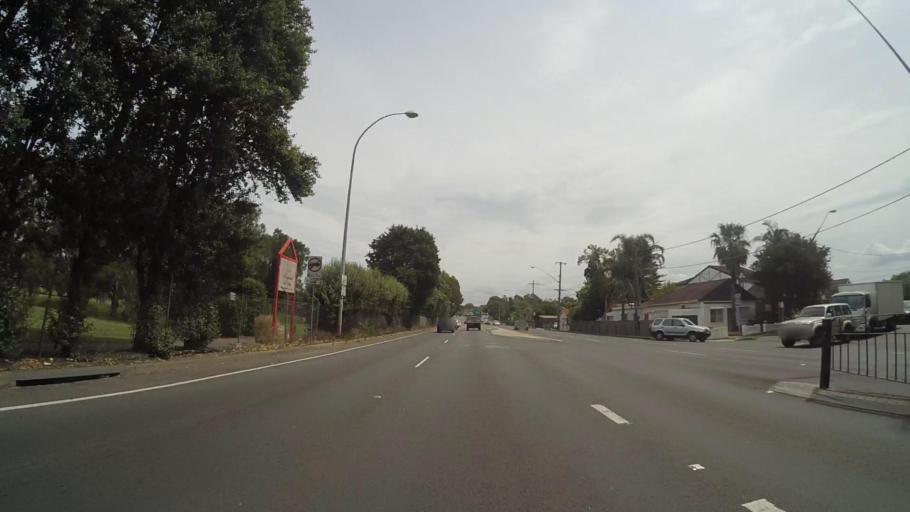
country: AU
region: New South Wales
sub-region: Rockdale
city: Arncliffe
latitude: -33.9355
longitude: 151.1565
